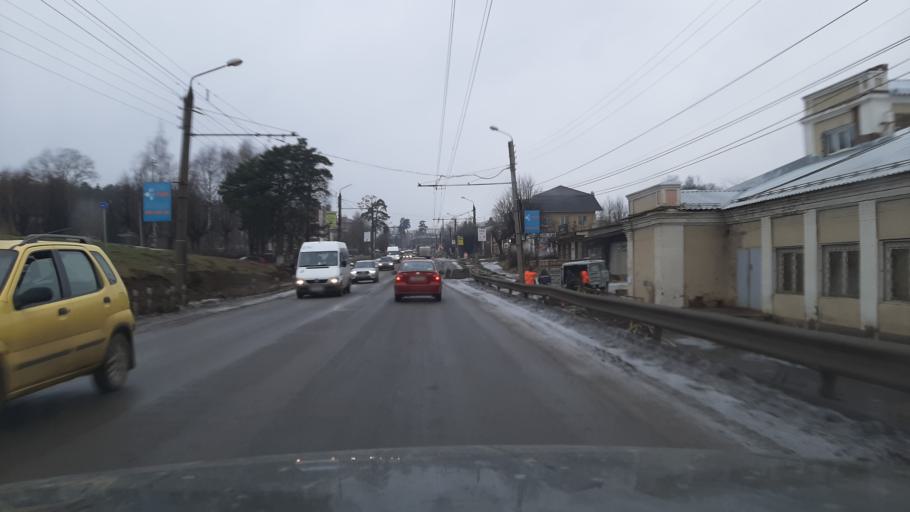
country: RU
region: Ivanovo
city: Kokhma
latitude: 56.9314
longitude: 41.0797
